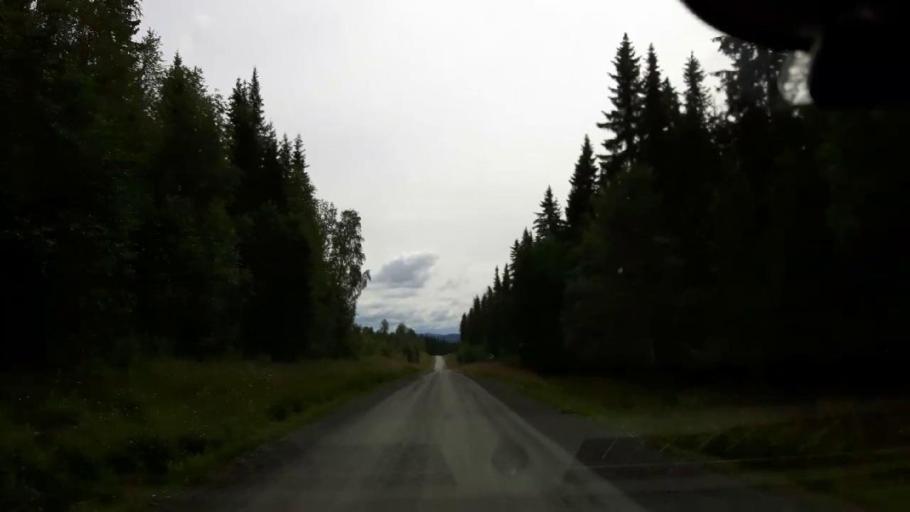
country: SE
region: Jaemtland
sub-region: Krokoms Kommun
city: Valla
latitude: 63.6493
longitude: 13.9866
